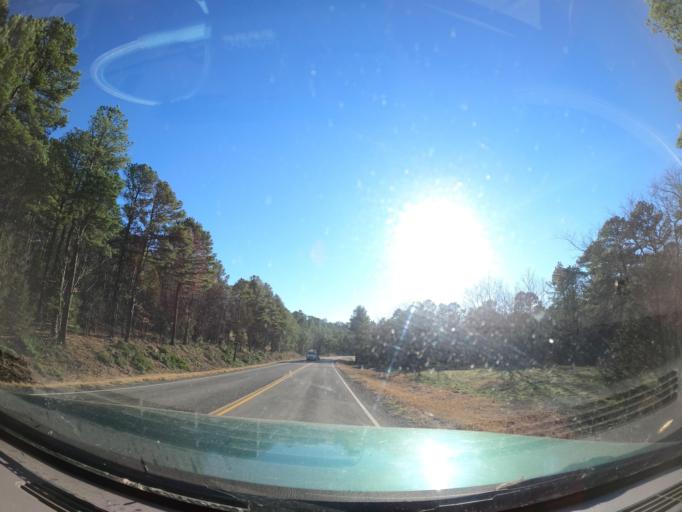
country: US
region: Oklahoma
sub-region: Latimer County
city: Wilburton
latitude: 34.9870
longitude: -95.3530
